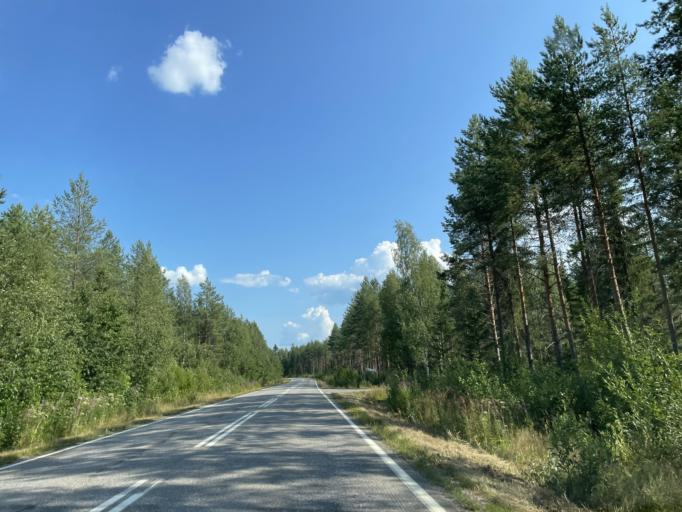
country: FI
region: Central Finland
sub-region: Saarijaervi-Viitasaari
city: Pihtipudas
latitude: 63.3637
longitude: 25.7171
